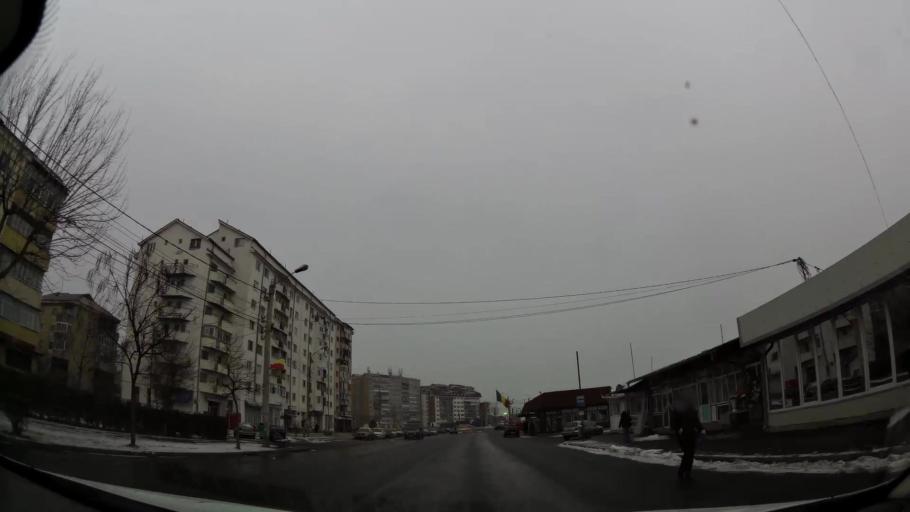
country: RO
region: Dambovita
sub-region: Municipiul Targoviste
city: Targoviste
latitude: 44.9296
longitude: 25.4386
